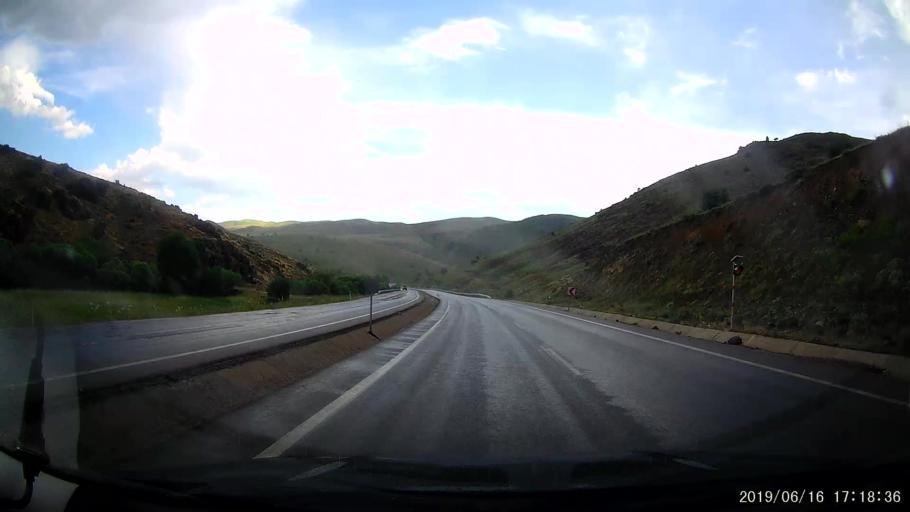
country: TR
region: Erzincan
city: Tercan
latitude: 39.8118
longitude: 40.5288
